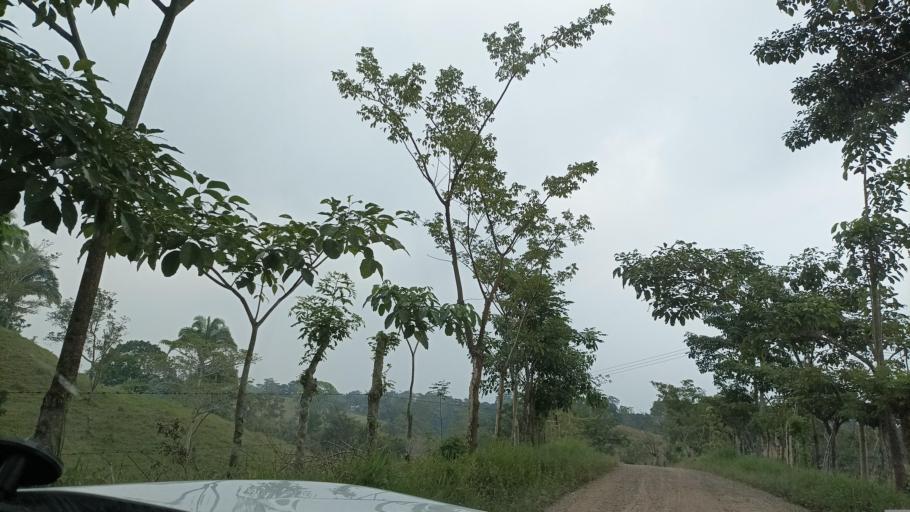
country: MX
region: Veracruz
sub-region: Uxpanapa
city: Poblado 10
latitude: 17.5721
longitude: -94.2280
